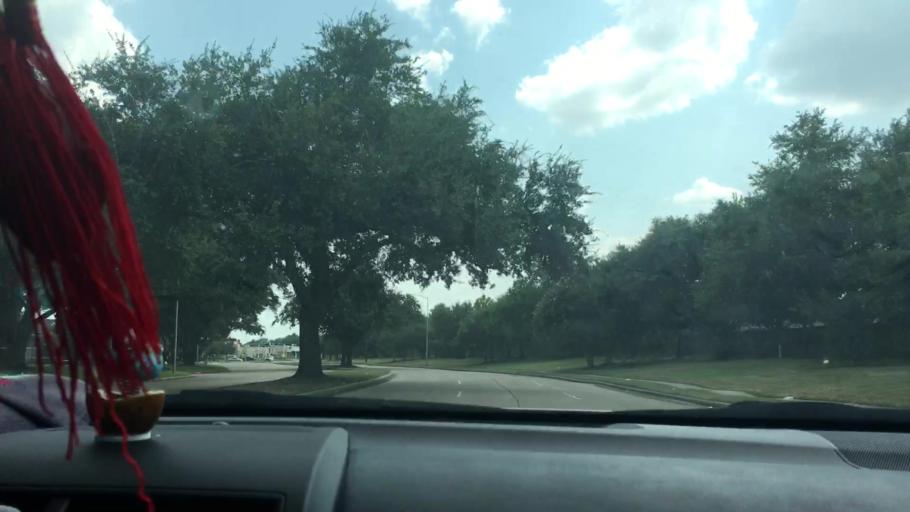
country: US
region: Texas
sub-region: Fort Bend County
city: Mission Bend
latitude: 29.7320
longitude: -95.6366
